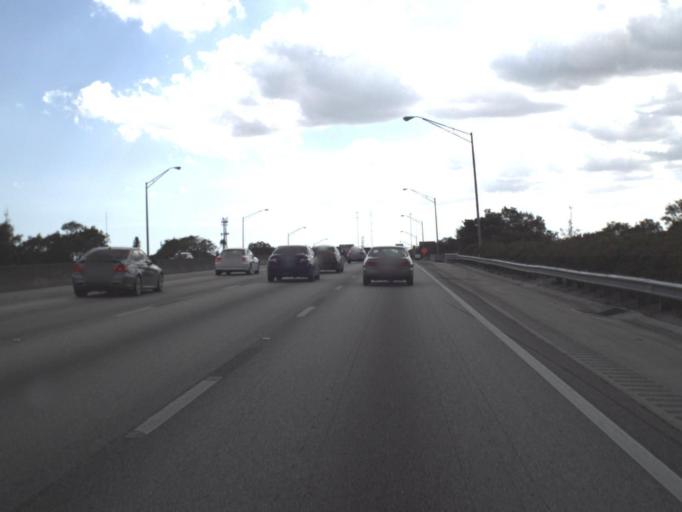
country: US
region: Florida
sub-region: Broward County
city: Pembroke Pines
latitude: 26.0259
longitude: -80.2133
